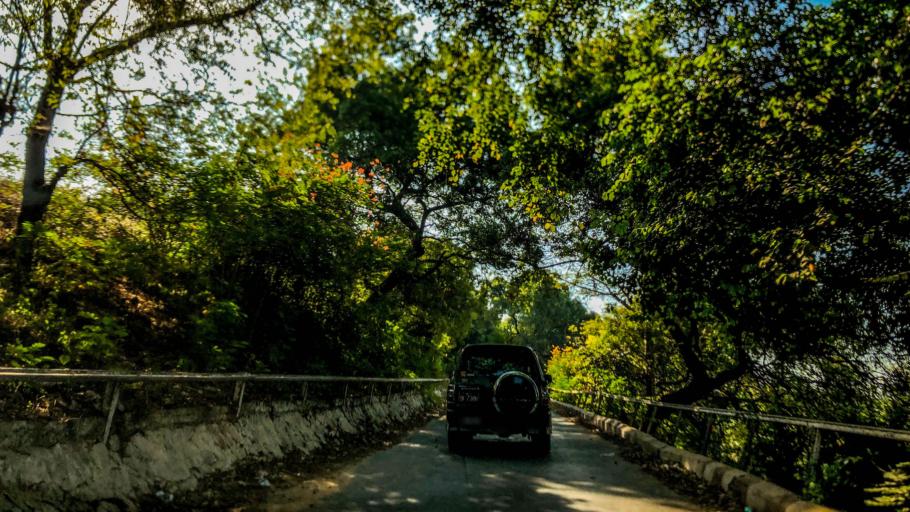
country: MM
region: Sagain
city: Sagaing
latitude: 21.8773
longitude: 95.9863
